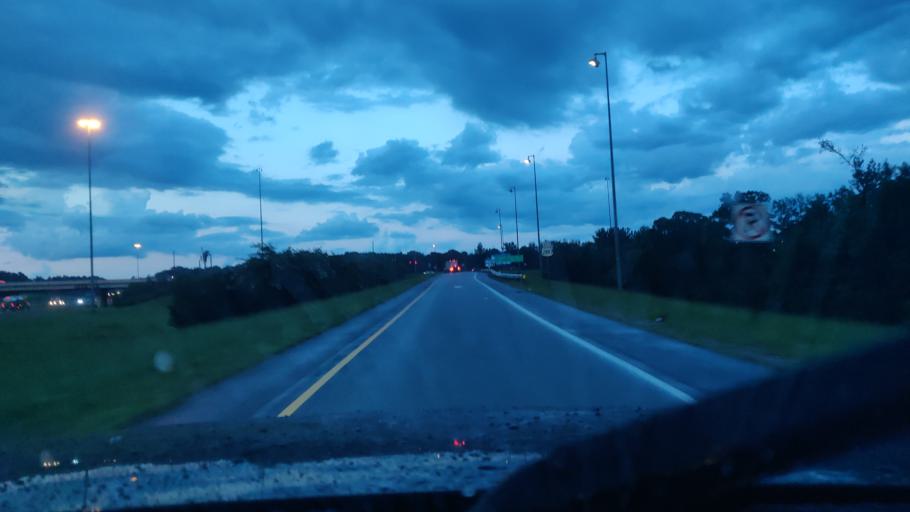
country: US
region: Alabama
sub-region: Lee County
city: Opelika
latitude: 32.6151
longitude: -85.4039
